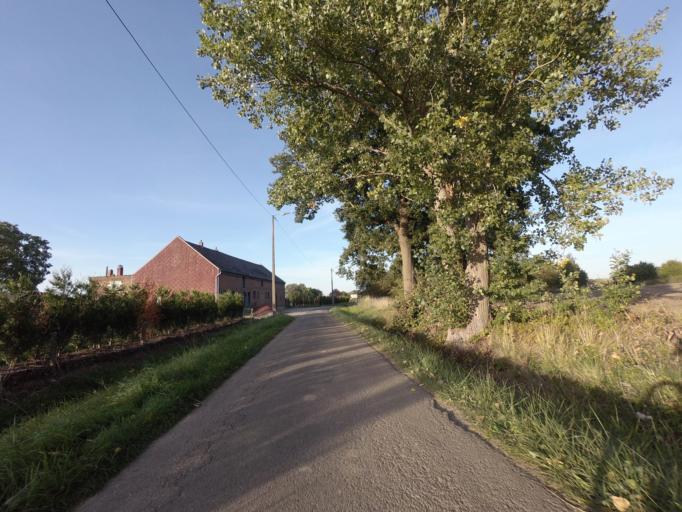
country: BE
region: Flanders
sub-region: Provincie Vlaams-Brabant
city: Boortmeerbeek
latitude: 50.9422
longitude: 4.6006
